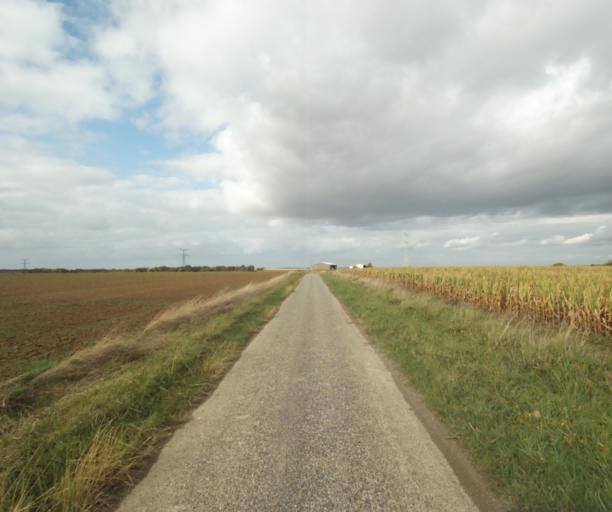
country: FR
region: Midi-Pyrenees
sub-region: Departement du Tarn-et-Garonne
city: Beaumont-de-Lomagne
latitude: 43.9021
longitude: 1.1033
